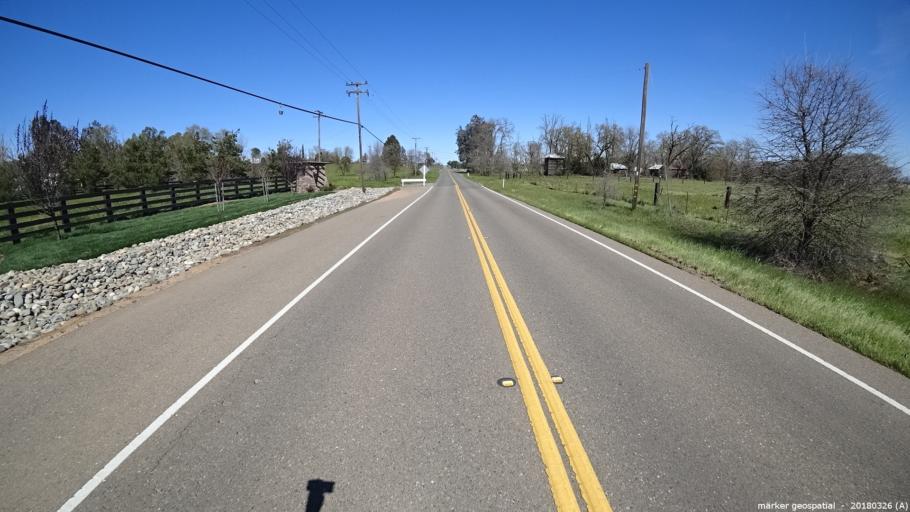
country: US
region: California
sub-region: Sacramento County
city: Wilton
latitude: 38.4725
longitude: -121.2278
